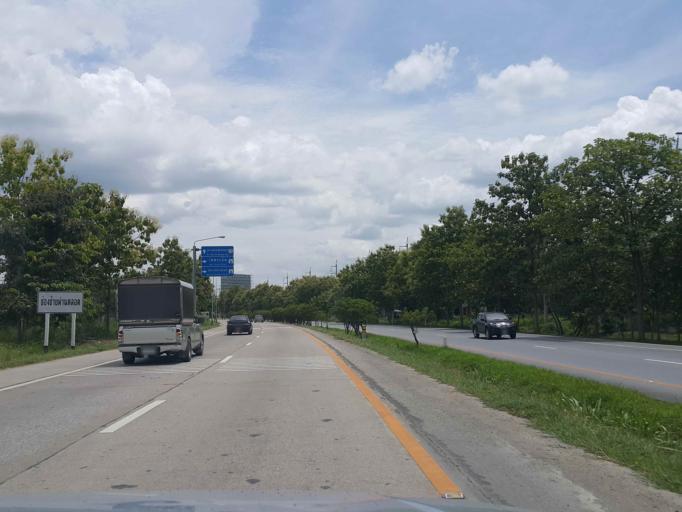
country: TH
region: Lamphun
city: Lamphun
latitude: 18.5576
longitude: 99.0461
